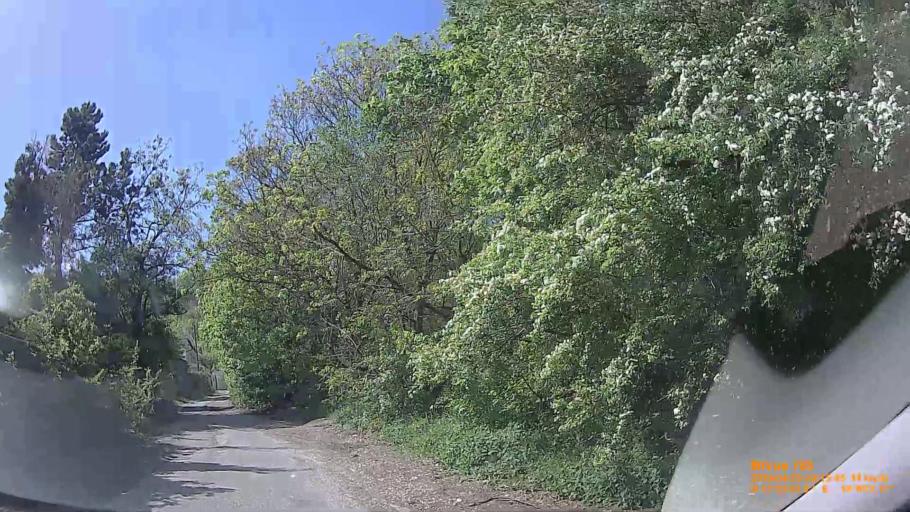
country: HU
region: Pest
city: Urom
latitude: 47.5646
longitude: 19.0006
